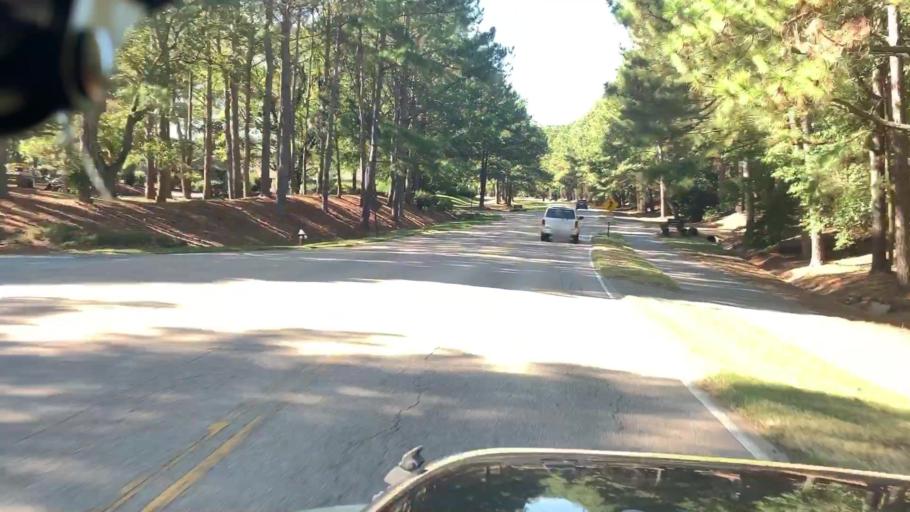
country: US
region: Virginia
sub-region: City of Williamsburg
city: Williamsburg
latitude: 37.2320
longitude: -76.6742
